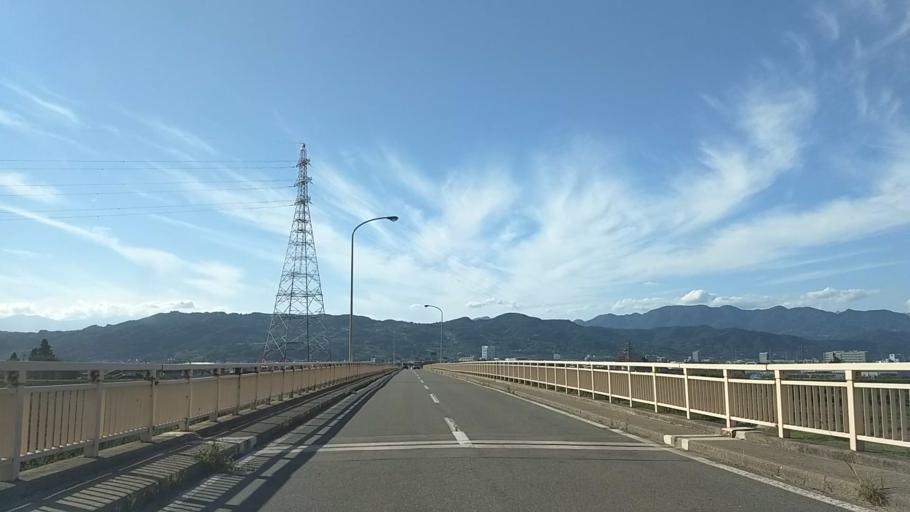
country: JP
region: Nagano
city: Nagano-shi
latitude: 36.5626
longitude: 138.1567
